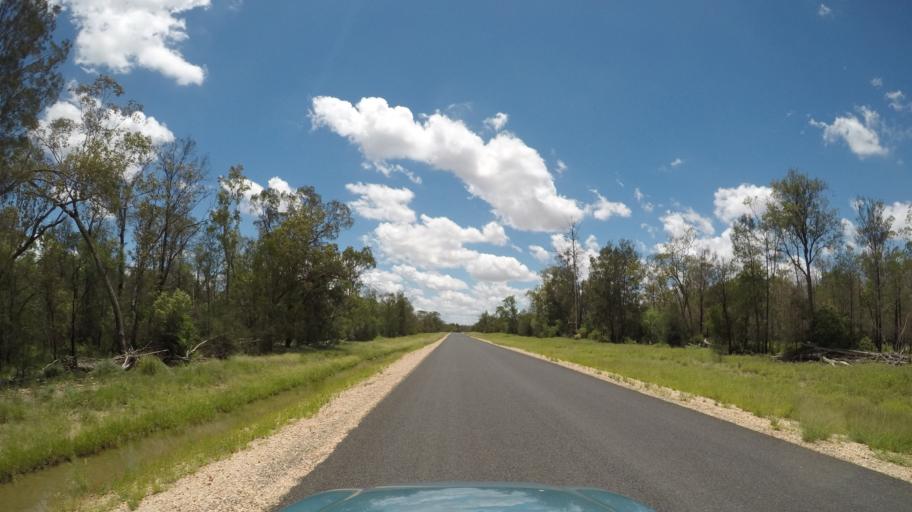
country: AU
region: Queensland
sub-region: Goondiwindi
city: Goondiwindi
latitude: -28.1539
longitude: 150.1236
